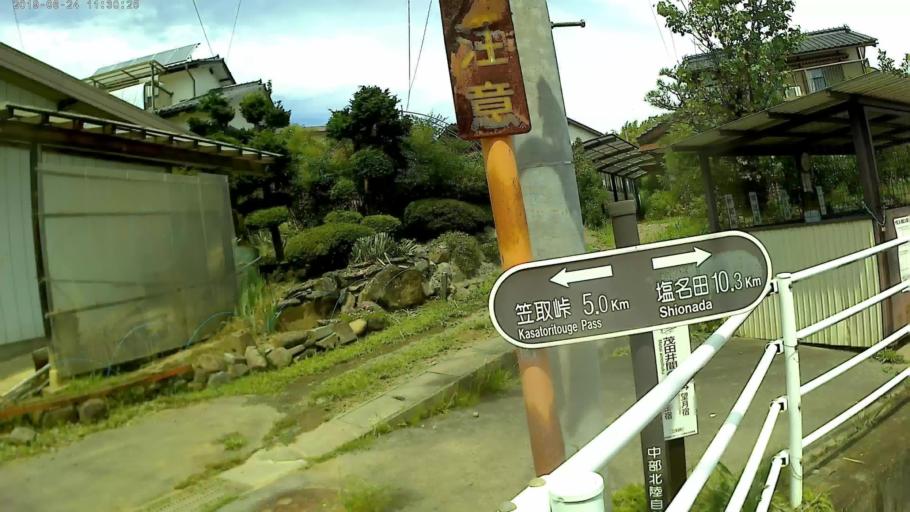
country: JP
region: Nagano
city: Kamimaruko
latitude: 36.2708
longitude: 138.3327
